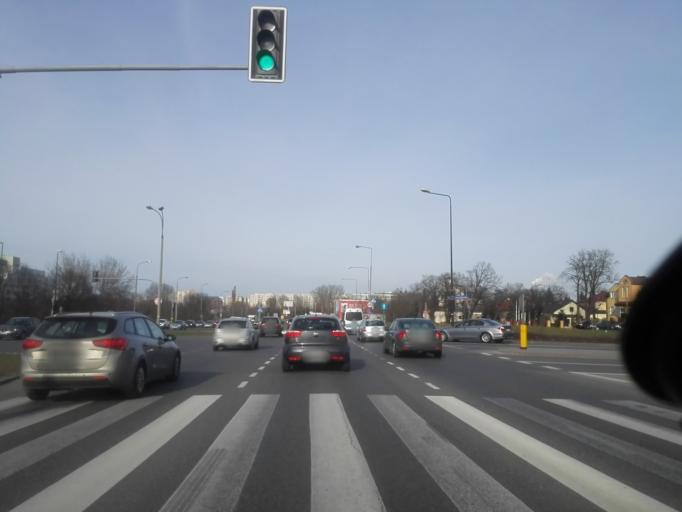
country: PL
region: Masovian Voivodeship
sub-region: Warszawa
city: Ursynow
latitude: 52.1699
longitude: 21.0404
